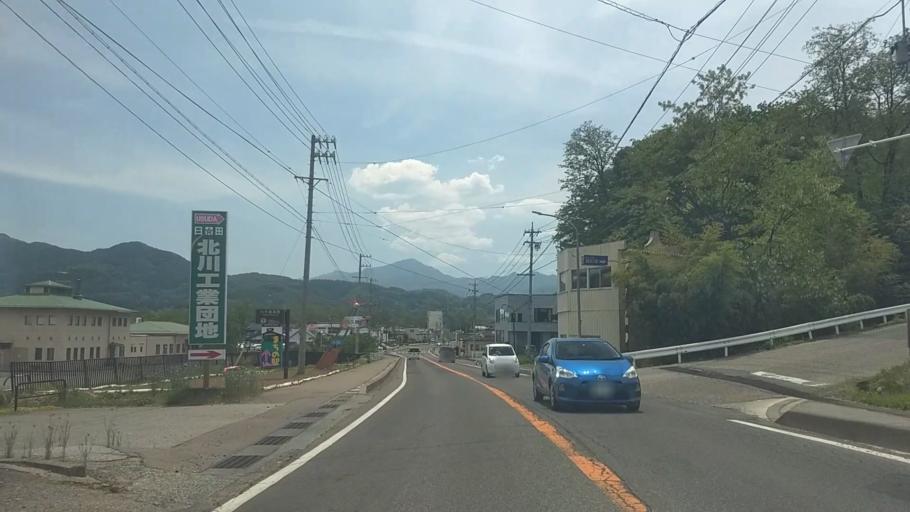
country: JP
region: Nagano
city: Saku
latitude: 36.1796
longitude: 138.4823
